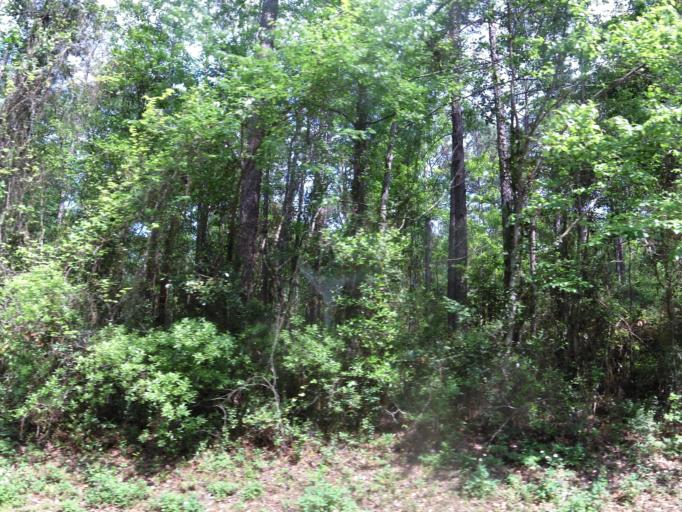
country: US
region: Georgia
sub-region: Camden County
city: Kingsland
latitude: 30.7819
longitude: -81.6960
